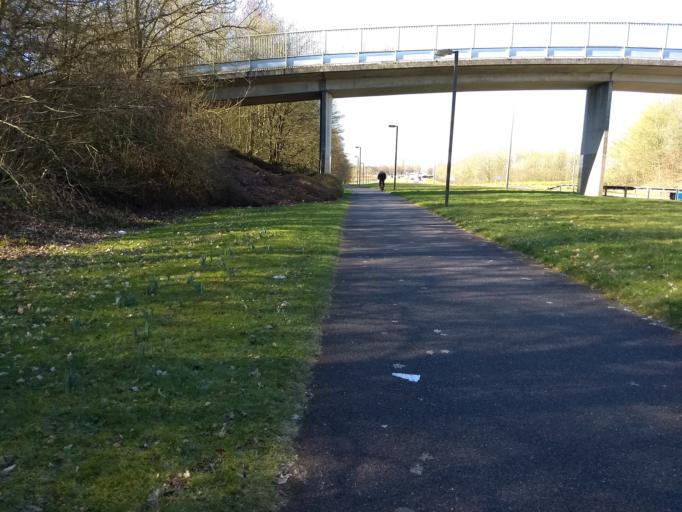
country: GB
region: England
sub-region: Milton Keynes
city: Shenley Church End
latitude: 52.0027
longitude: -0.7849
